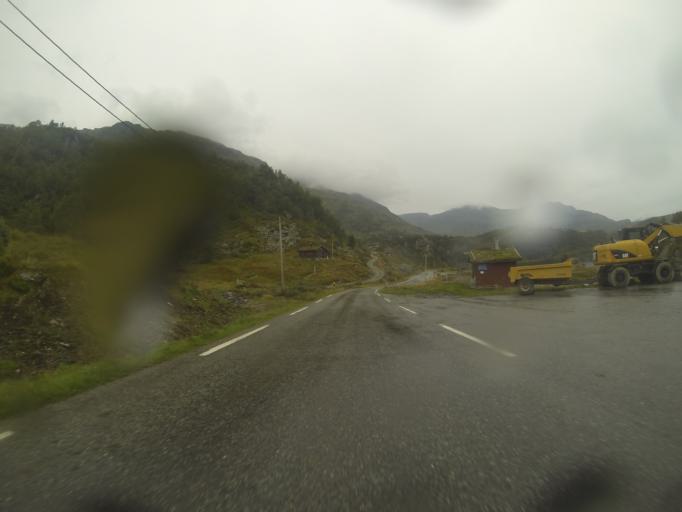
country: NO
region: Rogaland
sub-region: Sauda
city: Sauda
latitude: 59.7229
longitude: 6.5601
